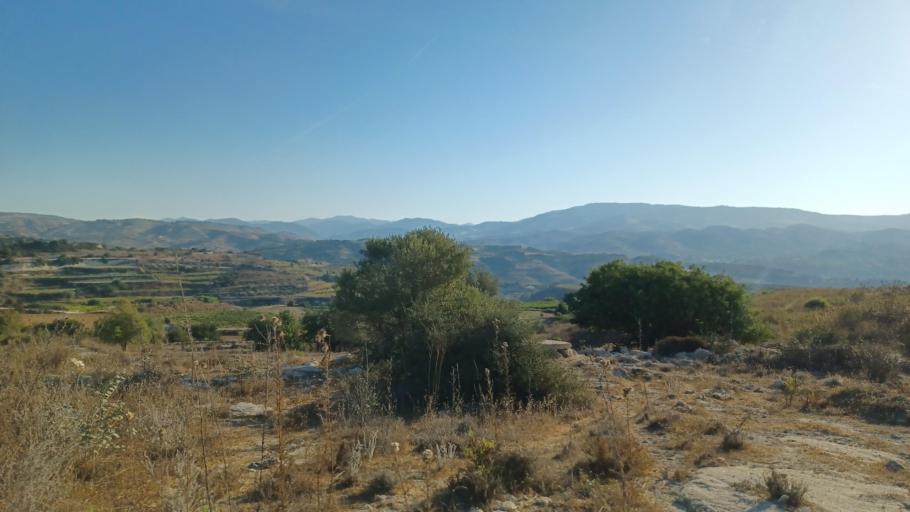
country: CY
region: Pafos
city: Mesogi
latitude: 34.8649
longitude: 32.5191
